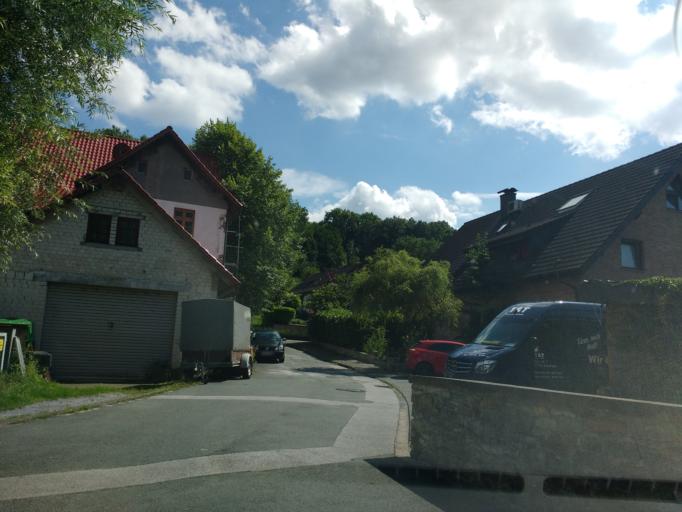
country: DE
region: North Rhine-Westphalia
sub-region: Regierungsbezirk Detmold
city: Schlangen
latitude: 51.8274
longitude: 8.8701
